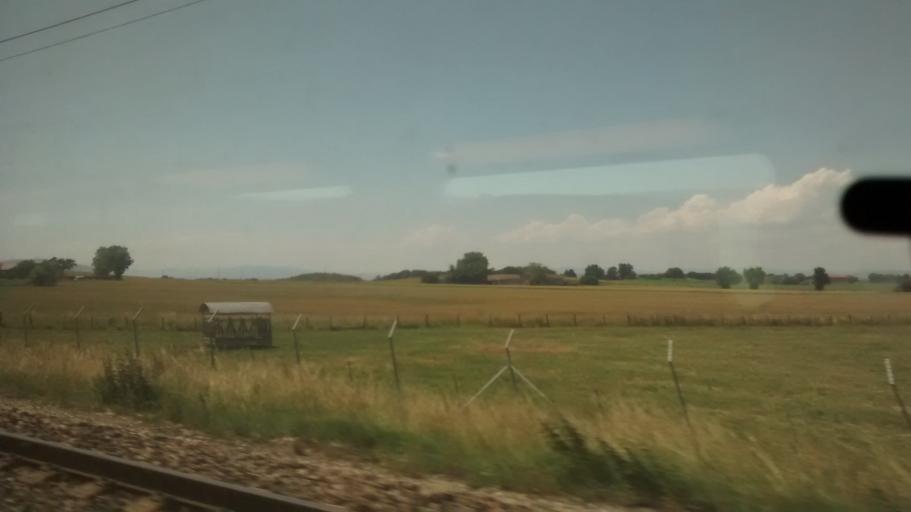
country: FR
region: Rhone-Alpes
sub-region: Departement de l'Ain
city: Ars-sur-Formans
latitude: 45.9726
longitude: 4.8625
